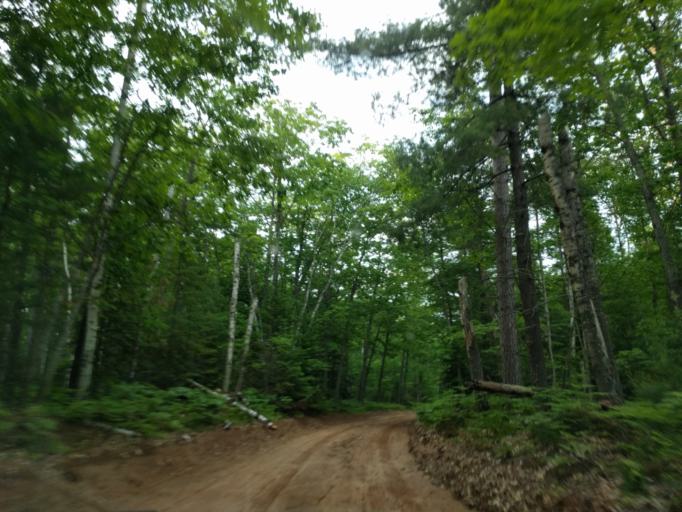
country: US
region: Michigan
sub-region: Marquette County
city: Trowbridge Park
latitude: 46.6179
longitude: -87.5028
